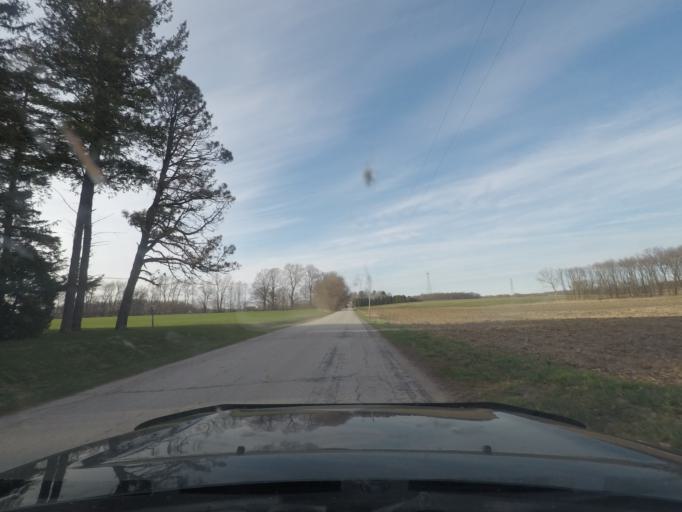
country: US
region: Indiana
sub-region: LaPorte County
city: Westville
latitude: 41.5414
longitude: -86.7987
